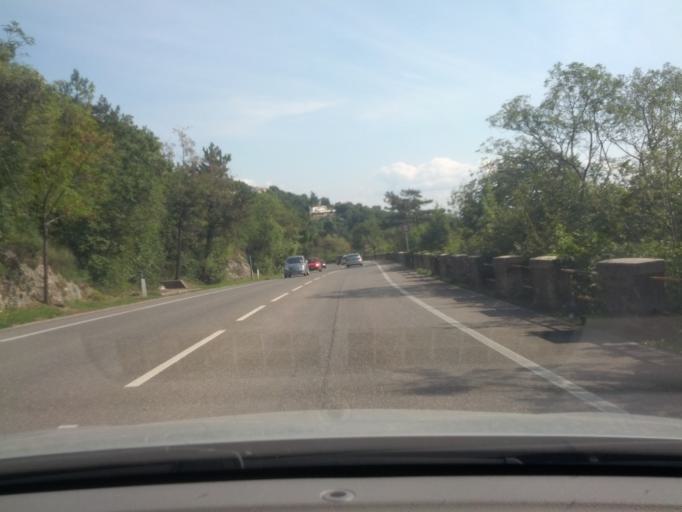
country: IT
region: Friuli Venezia Giulia
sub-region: Provincia di Trieste
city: Villa Opicina
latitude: 45.6769
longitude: 13.7873
